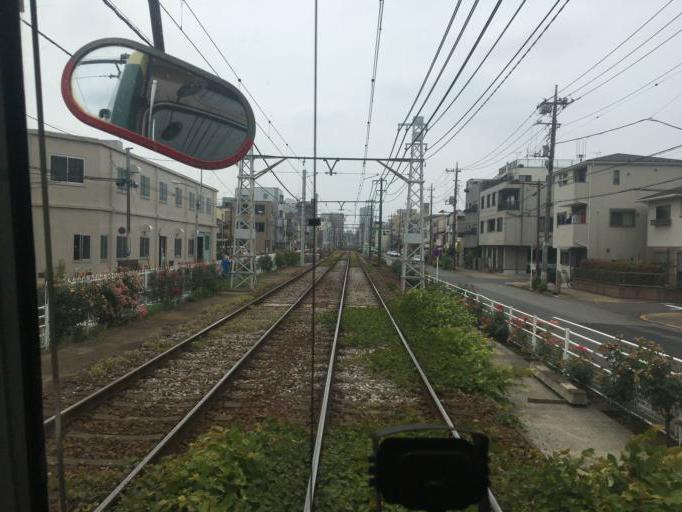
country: JP
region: Saitama
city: Kawaguchi
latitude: 35.7508
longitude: 139.7555
